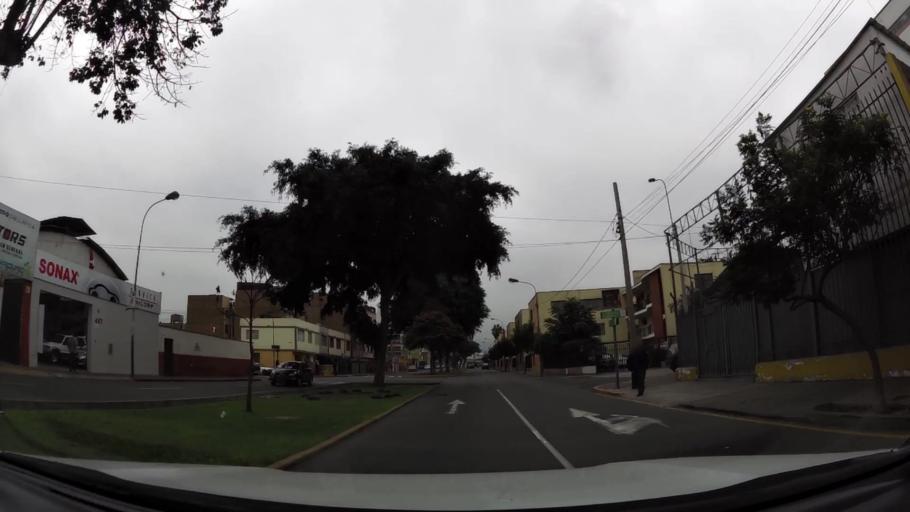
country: PE
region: Lima
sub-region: Lima
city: Surco
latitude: -12.1196
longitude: -77.0206
